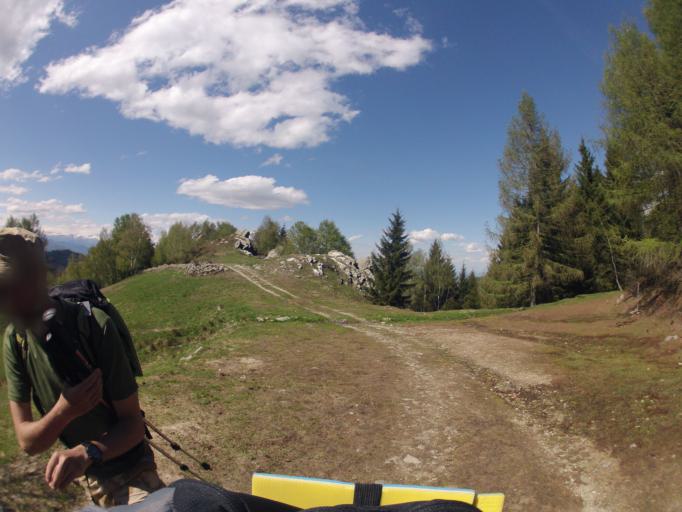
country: IT
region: Piedmont
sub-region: Provincia di Cuneo
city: Peveragno
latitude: 44.2789
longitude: 7.5846
